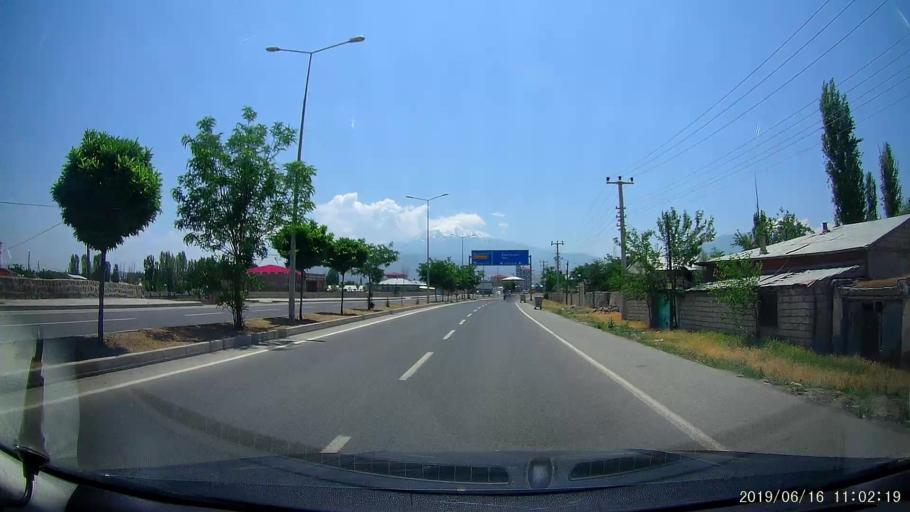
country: TR
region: Igdir
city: Igdir
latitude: 39.9077
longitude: 44.0585
